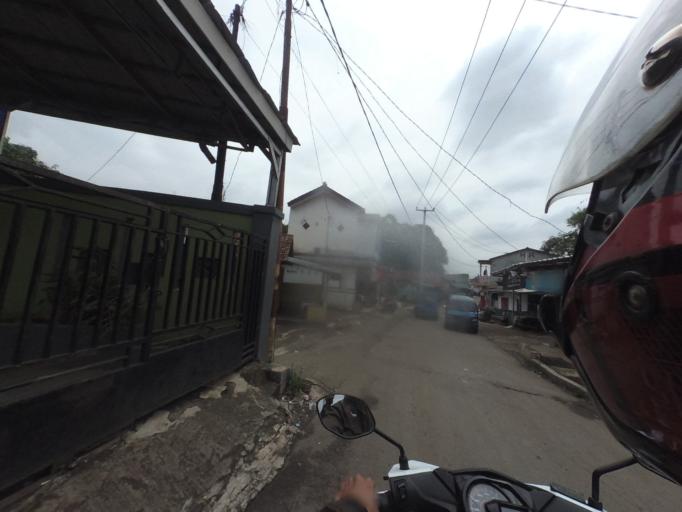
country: ID
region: West Java
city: Bogor
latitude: -6.6100
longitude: 106.7550
